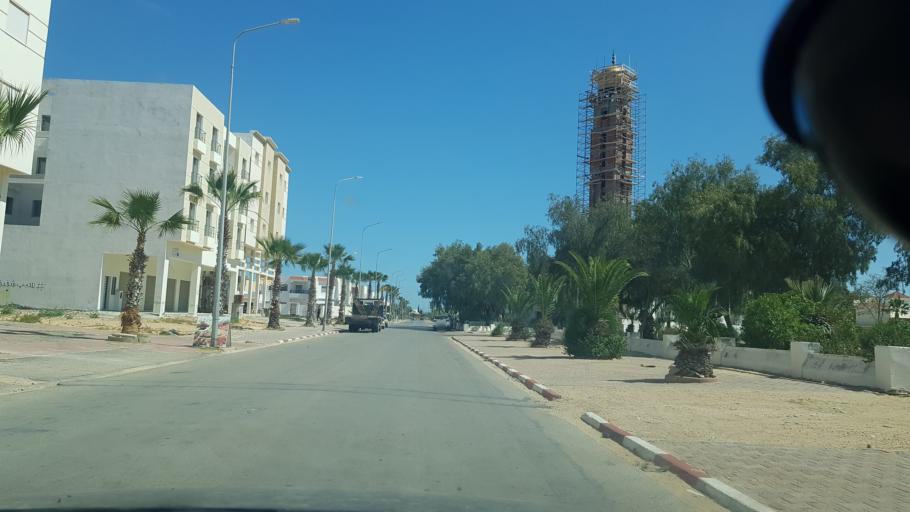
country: TN
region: Safaqis
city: Al Qarmadah
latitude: 34.8277
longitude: 10.7586
